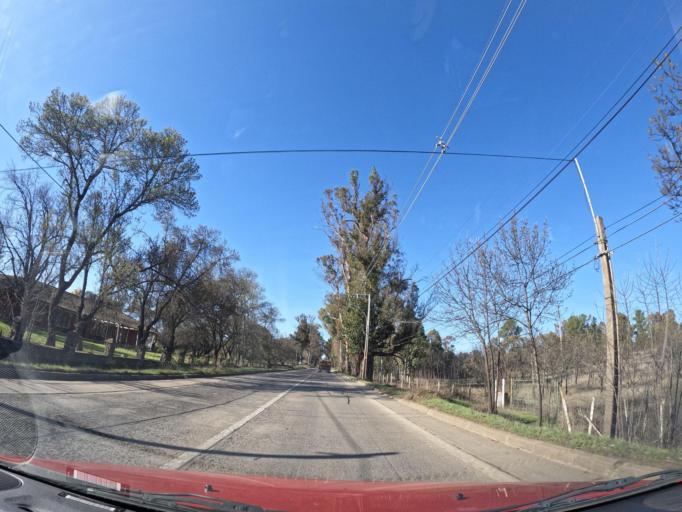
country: CL
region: Maule
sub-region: Provincia de Cauquenes
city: Cauquenes
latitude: -35.9579
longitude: -72.2889
